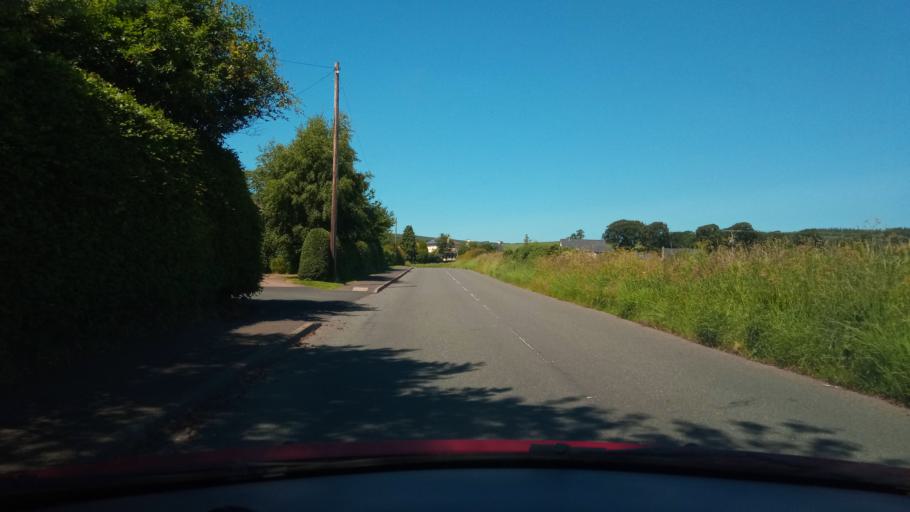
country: GB
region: Scotland
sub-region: The Scottish Borders
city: Duns
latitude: 55.7722
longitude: -2.3656
